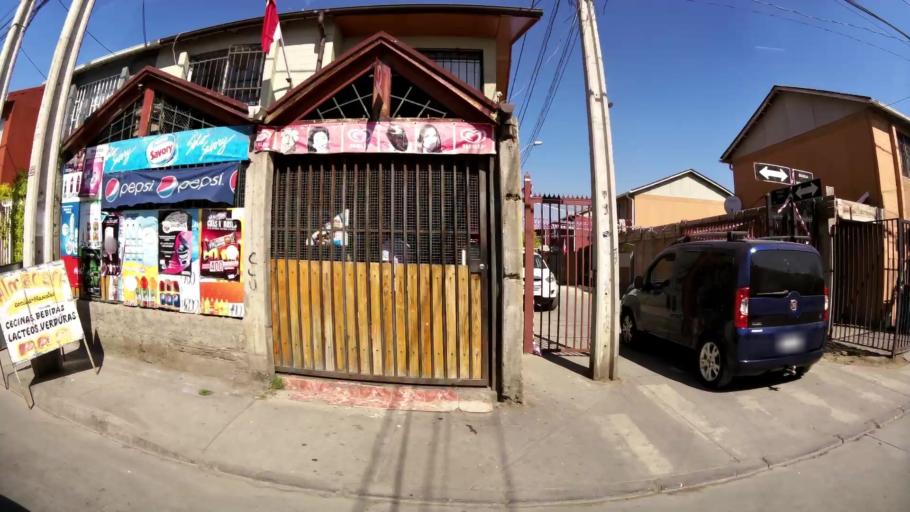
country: CL
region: Santiago Metropolitan
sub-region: Provincia de Santiago
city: Lo Prado
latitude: -33.3543
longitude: -70.7515
